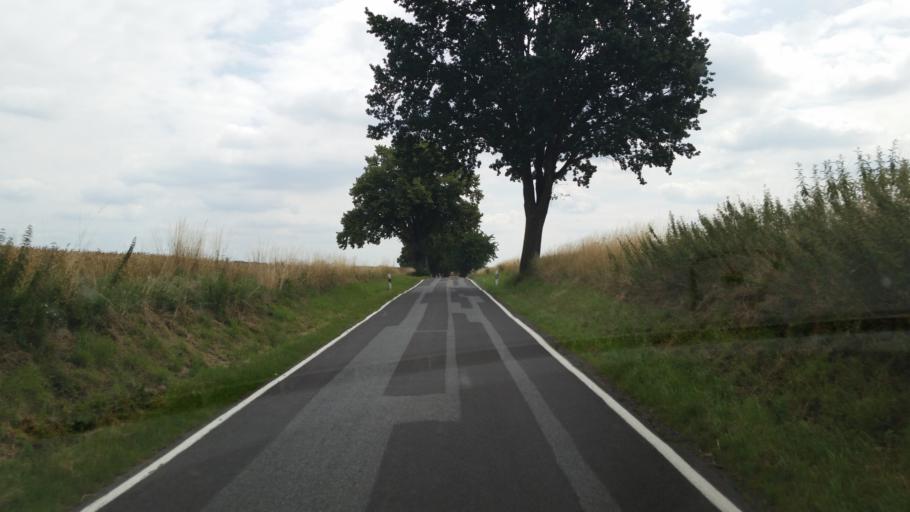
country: DE
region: Saxony
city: Crostwitz
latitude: 51.2275
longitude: 14.2750
